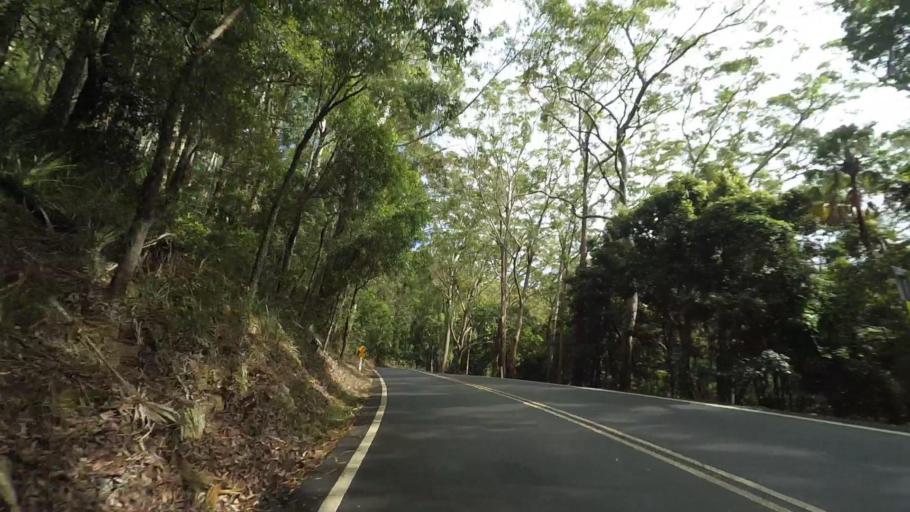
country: AU
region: New South Wales
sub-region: Wollongong
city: Helensburgh
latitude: -34.1962
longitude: 151.0112
